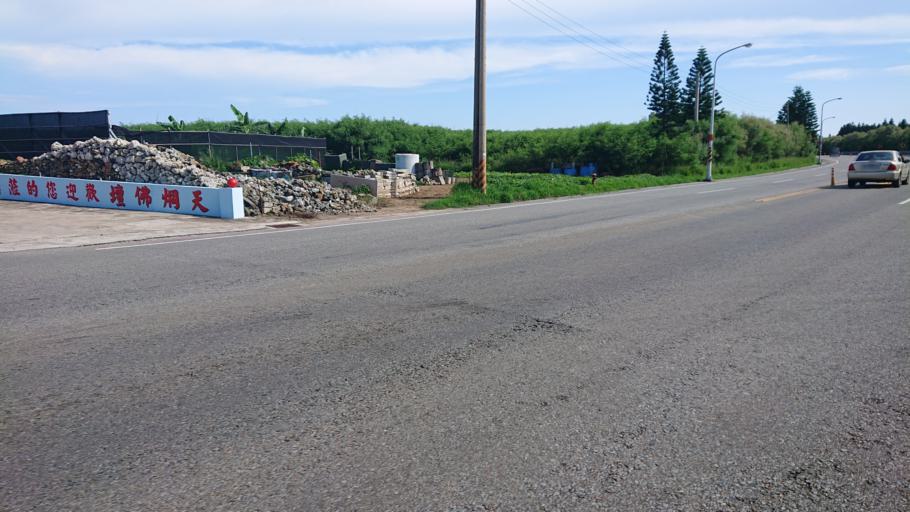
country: TW
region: Taiwan
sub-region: Penghu
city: Ma-kung
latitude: 23.5469
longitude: 119.6078
